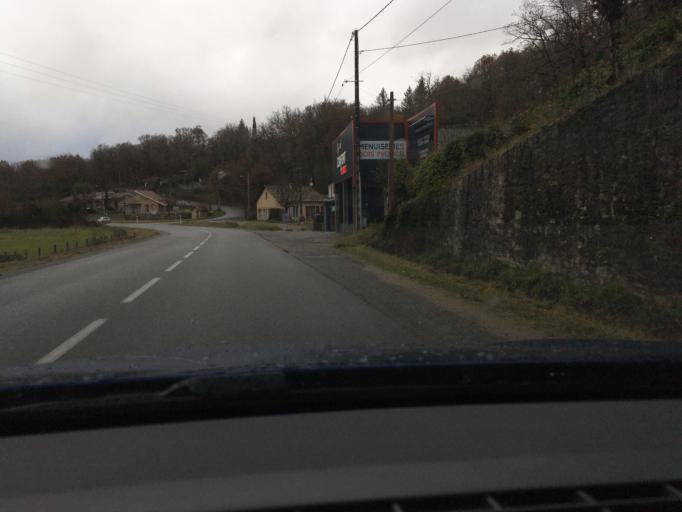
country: FR
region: Midi-Pyrenees
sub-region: Departement de l'Aveyron
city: Villefranche-de-Rouergue
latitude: 44.3697
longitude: 2.0161
